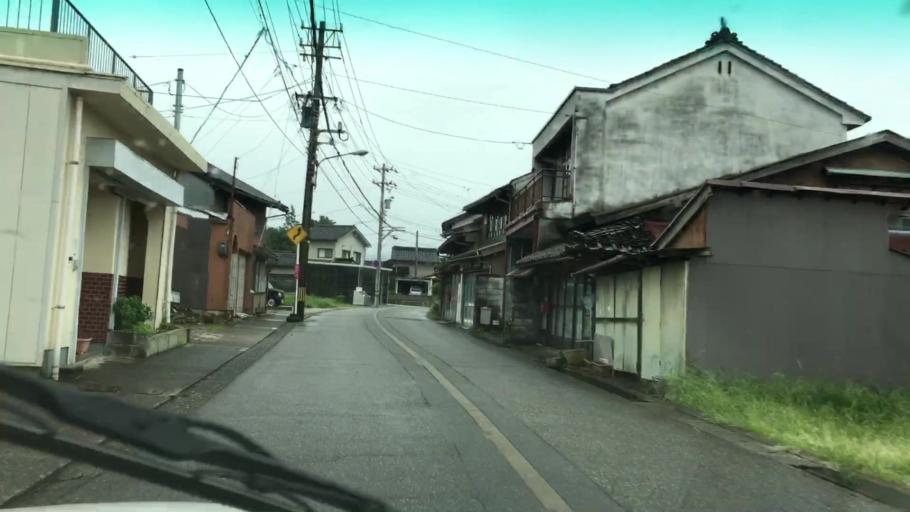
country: JP
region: Toyama
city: Kamiichi
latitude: 36.6580
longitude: 137.3183
